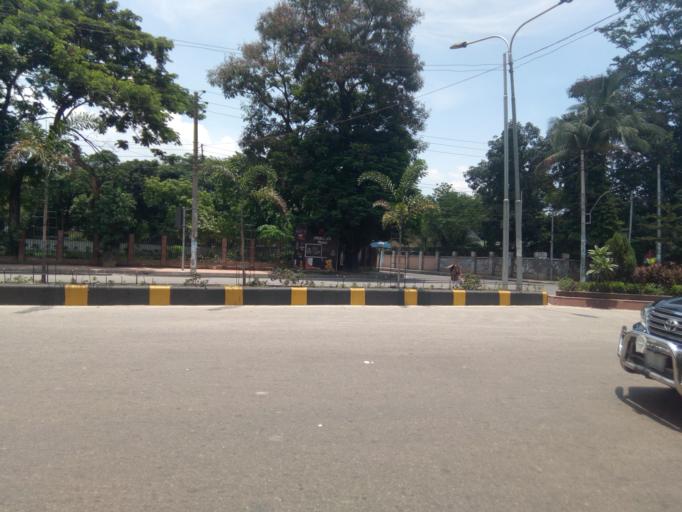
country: BD
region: Dhaka
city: Paltan
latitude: 23.7419
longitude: 90.3983
